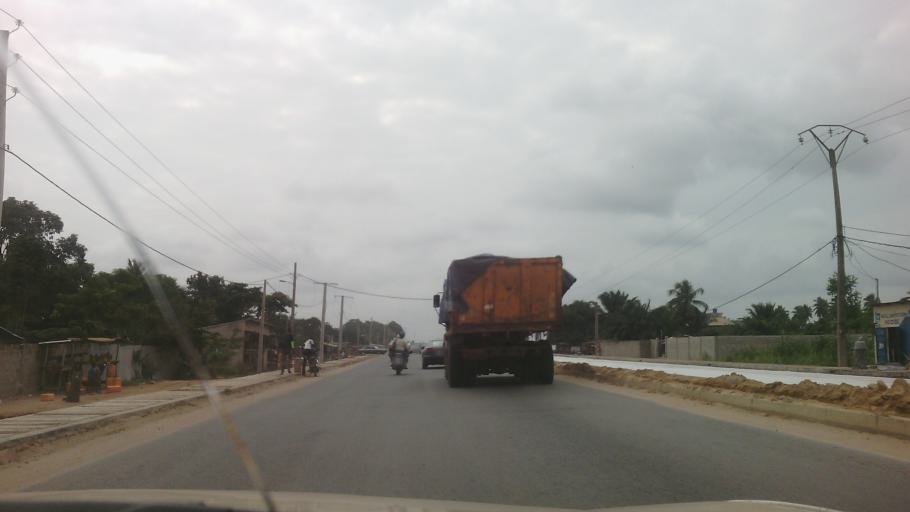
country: BJ
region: Atlantique
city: Hevie
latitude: 6.3835
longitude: 2.1884
